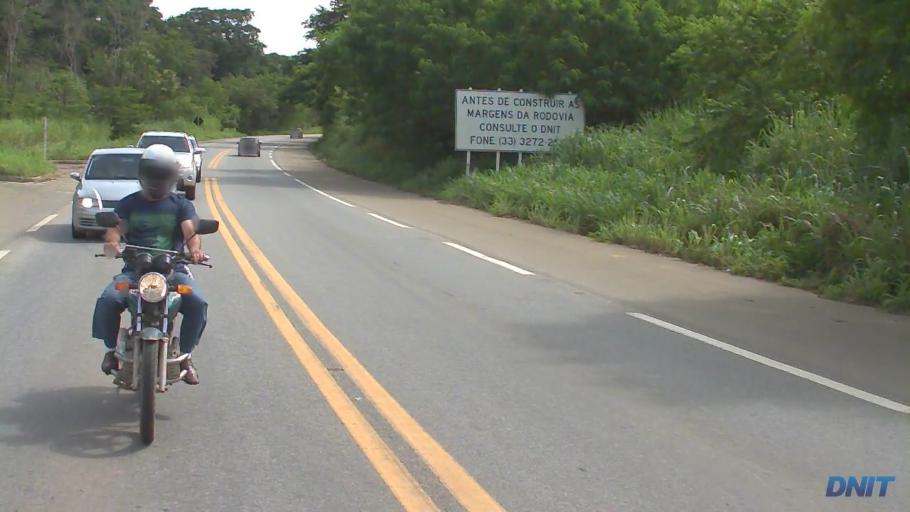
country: BR
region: Minas Gerais
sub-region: Ipaba
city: Ipaba
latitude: -19.3454
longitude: -42.4324
